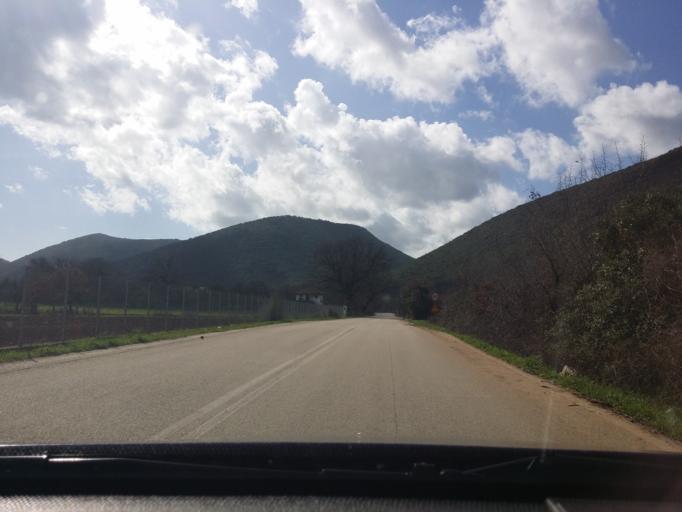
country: GR
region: West Greece
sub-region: Nomos Aitolias kai Akarnanias
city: Fitiai
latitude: 38.6195
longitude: 21.1460
